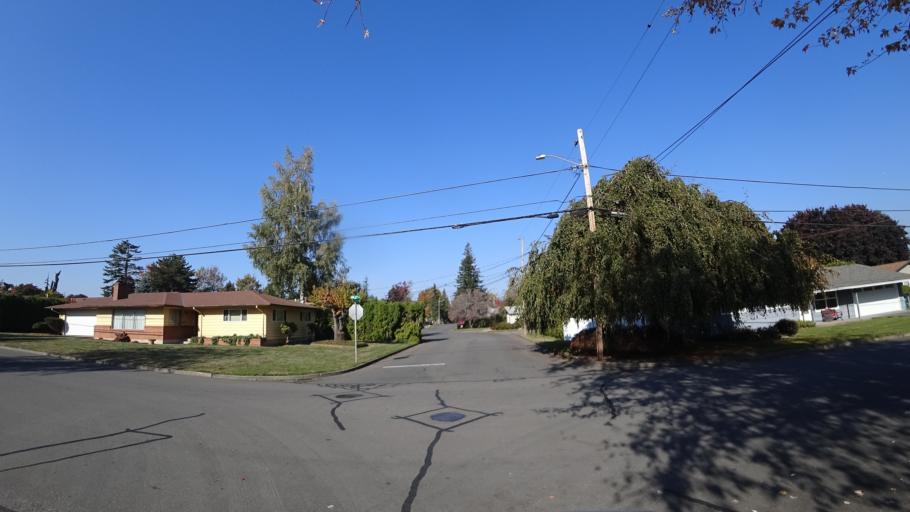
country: US
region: Oregon
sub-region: Multnomah County
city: Gresham
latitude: 45.5001
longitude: -122.4490
